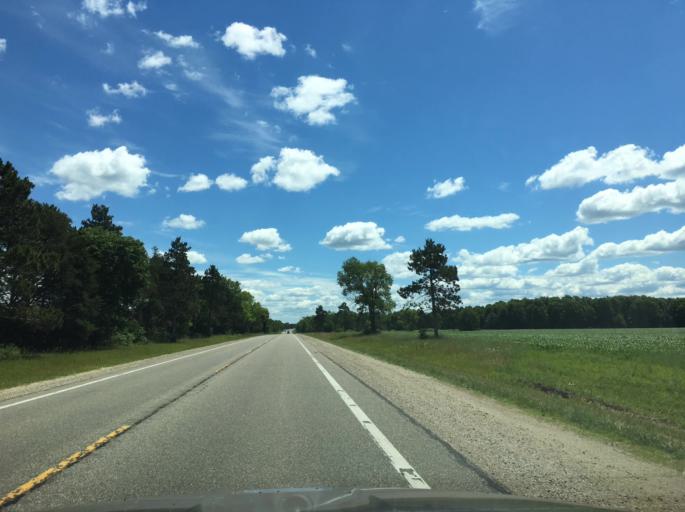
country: US
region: Michigan
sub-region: Osceola County
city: Reed City
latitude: 43.8726
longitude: -85.4209
